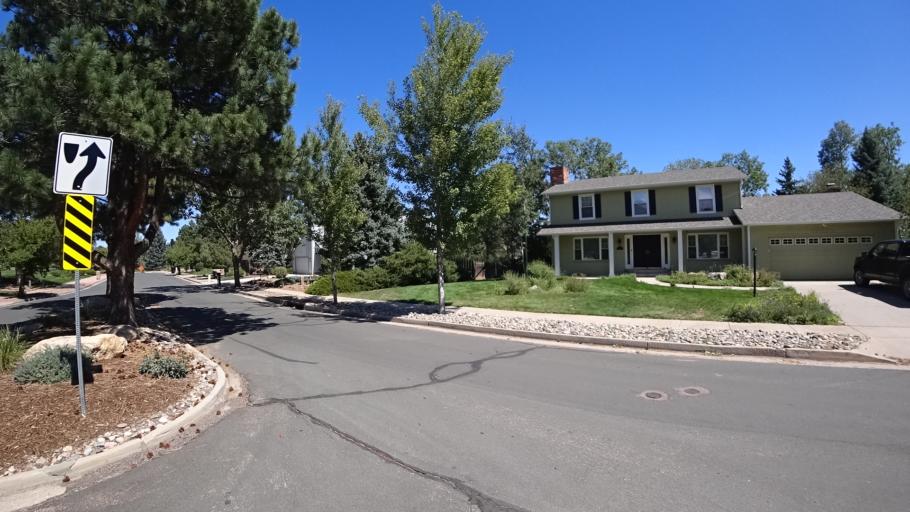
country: US
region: Colorado
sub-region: El Paso County
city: Colorado Springs
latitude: 38.7881
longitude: -104.8276
